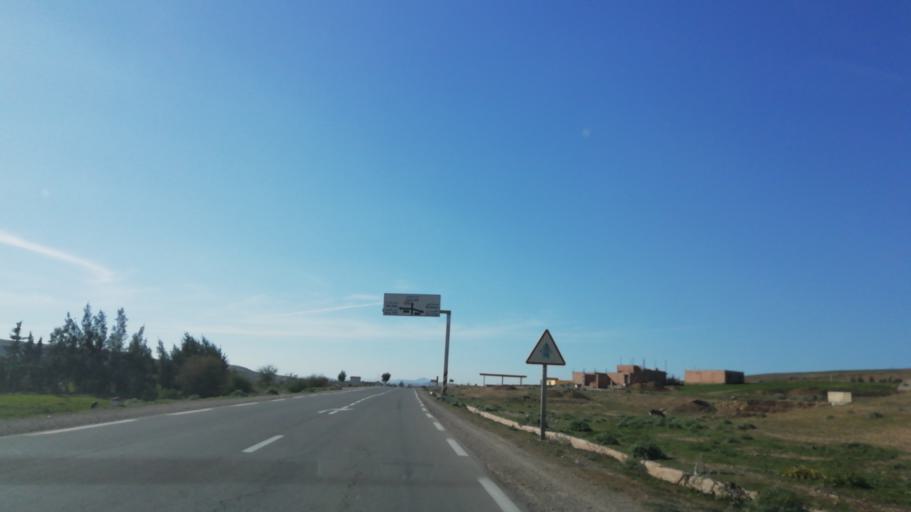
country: DZ
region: Mascara
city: Oued el Abtal
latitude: 35.4505
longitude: 0.7841
